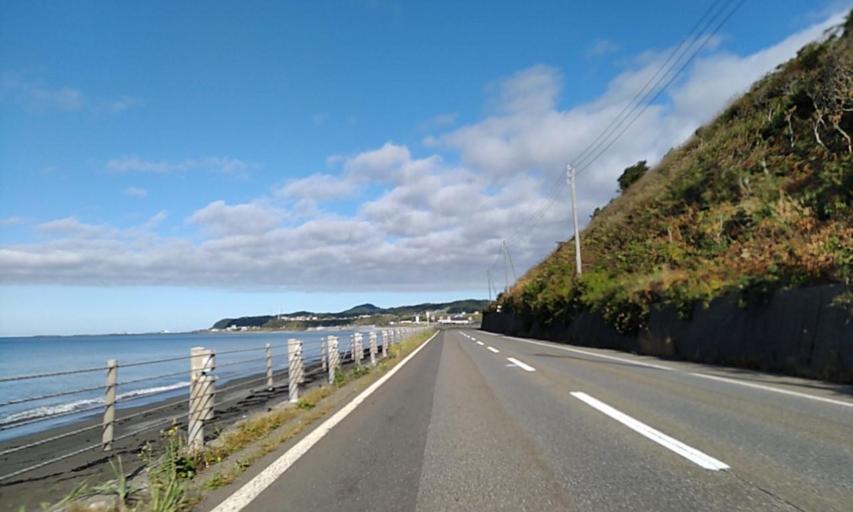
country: JP
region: Hokkaido
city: Shizunai-furukawacho
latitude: 42.2392
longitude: 142.5913
